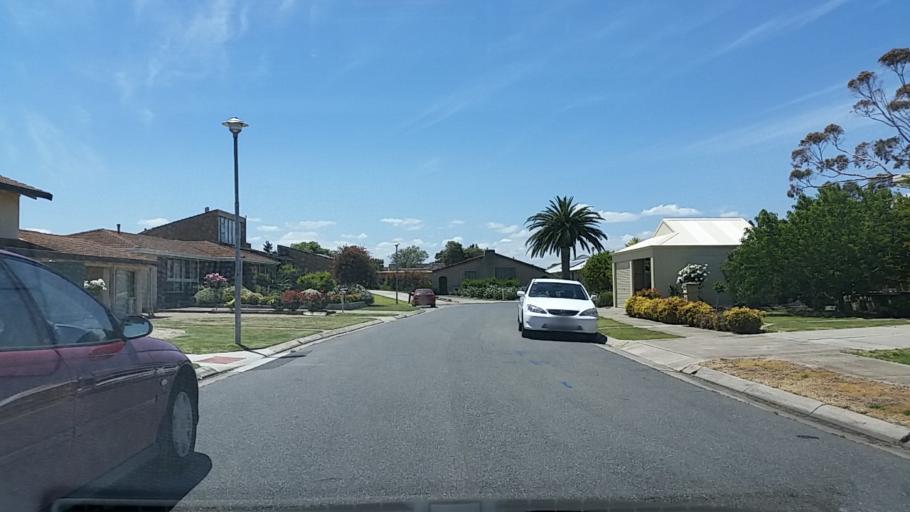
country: AU
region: South Australia
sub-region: Charles Sturt
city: Grange
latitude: -34.8949
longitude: 138.4927
